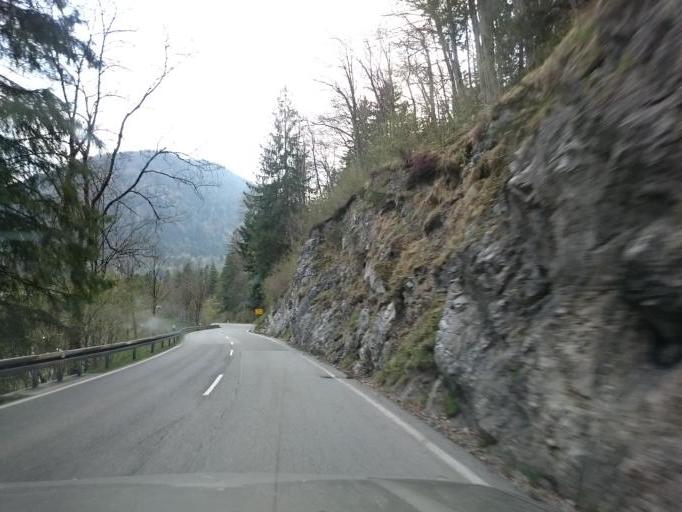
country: DE
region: Bavaria
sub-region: Upper Bavaria
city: Oberau
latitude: 47.5636
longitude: 11.1279
